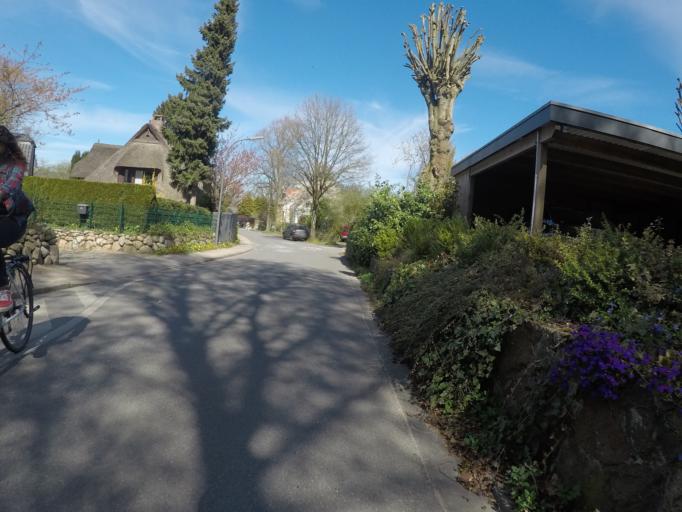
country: DE
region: Hamburg
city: Duvenstedt
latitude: 53.7034
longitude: 10.1146
